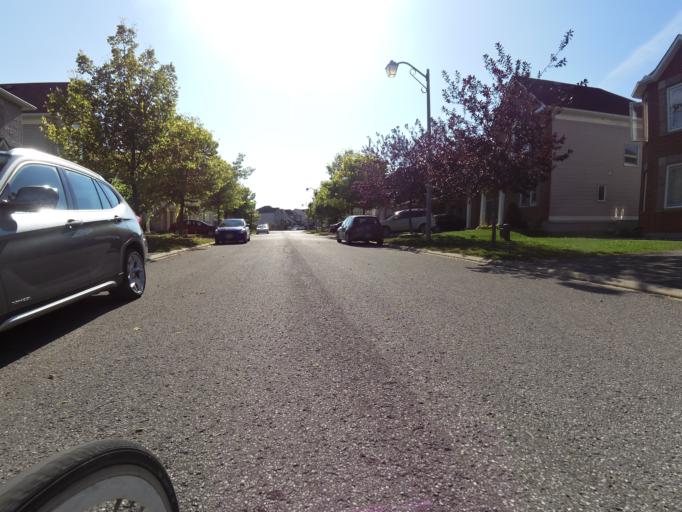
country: CA
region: Ontario
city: Bells Corners
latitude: 45.2710
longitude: -75.7100
